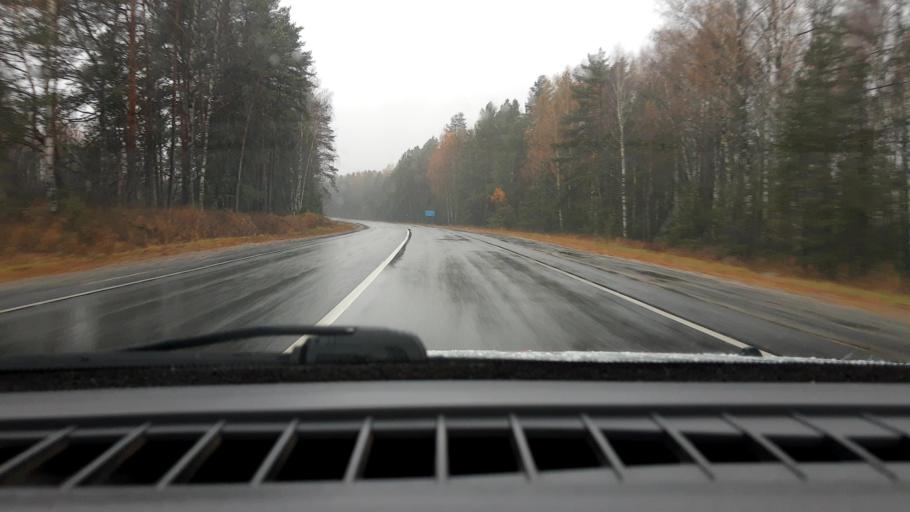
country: RU
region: Nizjnij Novgorod
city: Linda
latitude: 56.6798
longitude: 44.1517
